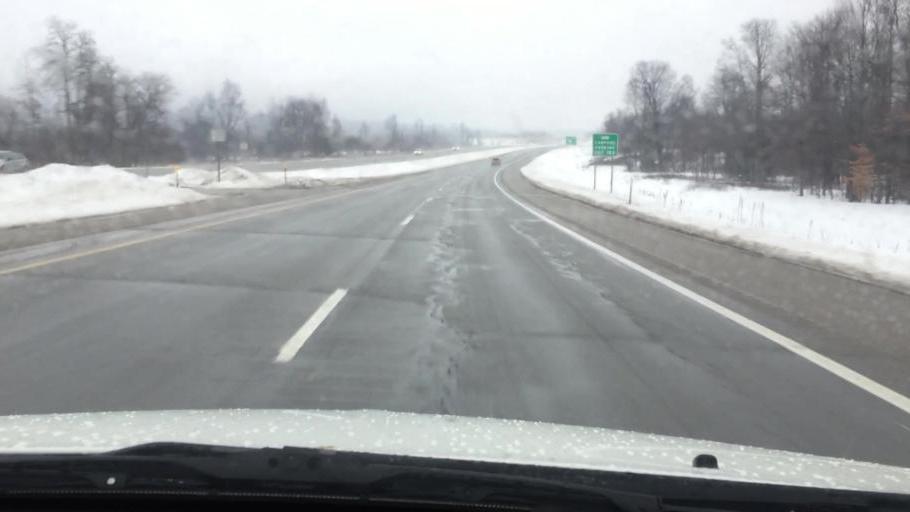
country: US
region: Michigan
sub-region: Wexford County
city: Cadillac
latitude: 44.2925
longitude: -85.3891
